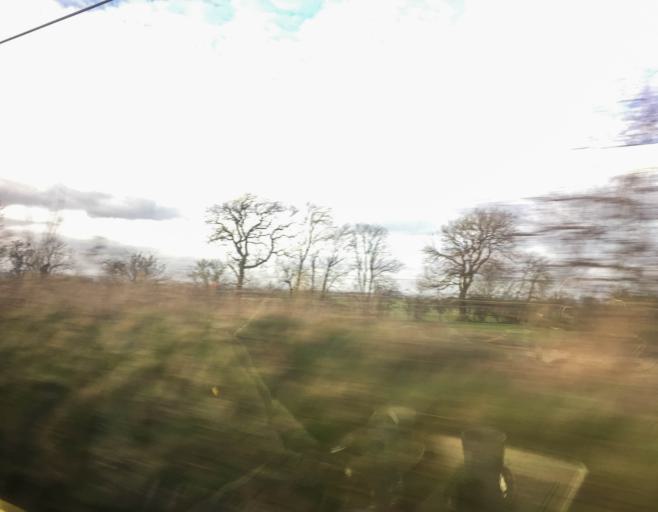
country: GB
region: Scotland
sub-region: Dumfries and Galloway
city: Gretna
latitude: 55.0111
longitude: -3.0568
